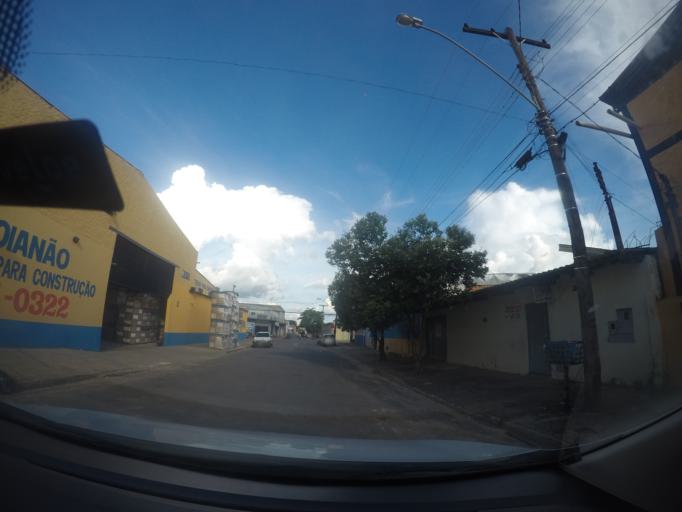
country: BR
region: Goias
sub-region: Goiania
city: Goiania
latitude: -16.6692
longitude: -49.3053
